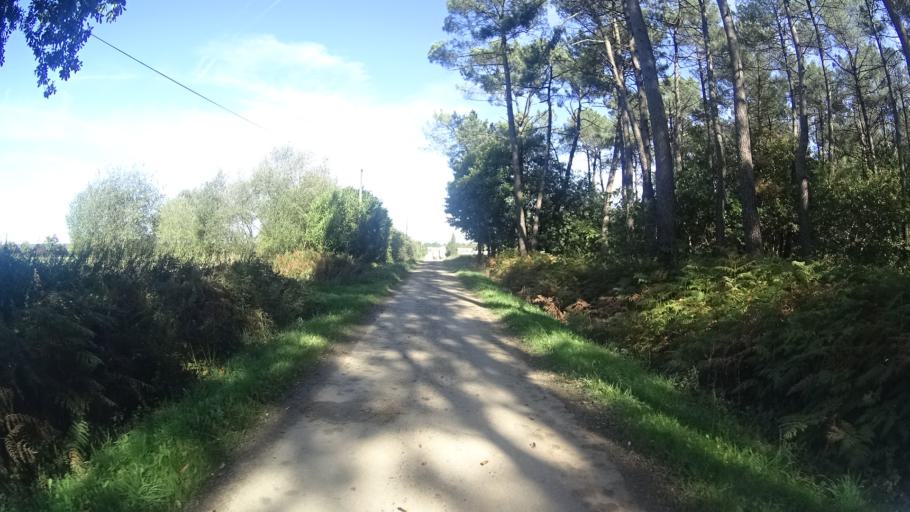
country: FR
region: Brittany
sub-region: Departement du Morbihan
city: La Gacilly
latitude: 47.7481
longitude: -2.1692
